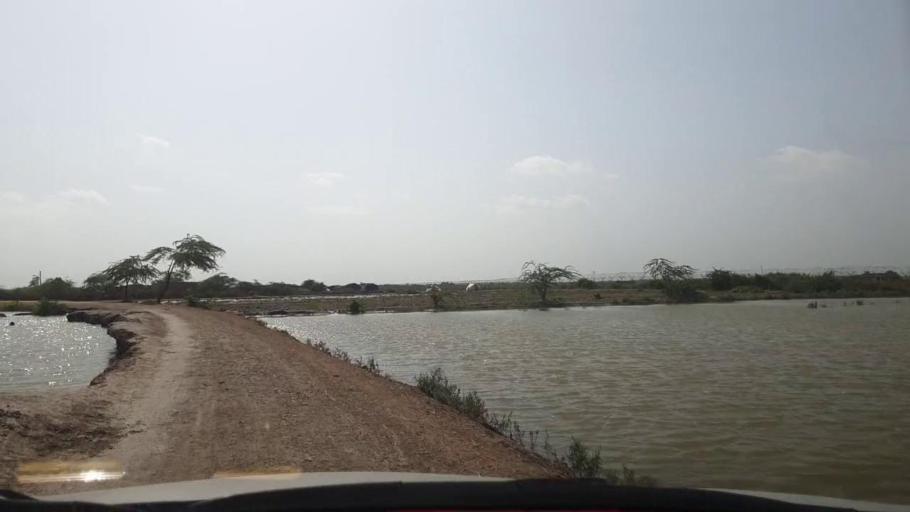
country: PK
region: Sindh
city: Talhar
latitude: 24.8382
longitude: 68.8459
